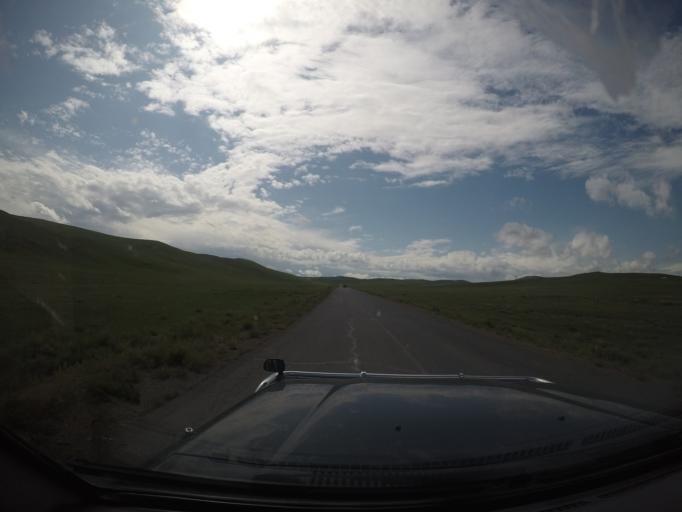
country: MN
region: Hentiy
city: Bayanbulag
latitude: 47.4565
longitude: 109.8167
